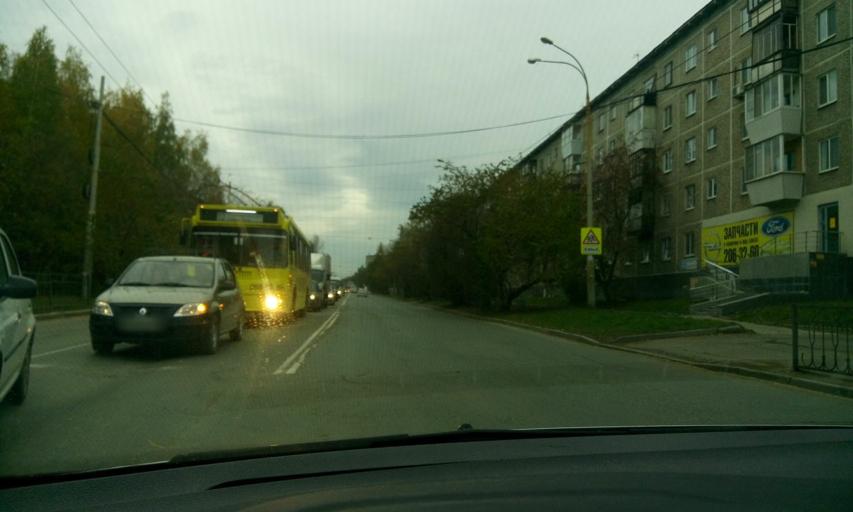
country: RU
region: Sverdlovsk
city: Yekaterinburg
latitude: 56.8607
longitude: 60.6534
